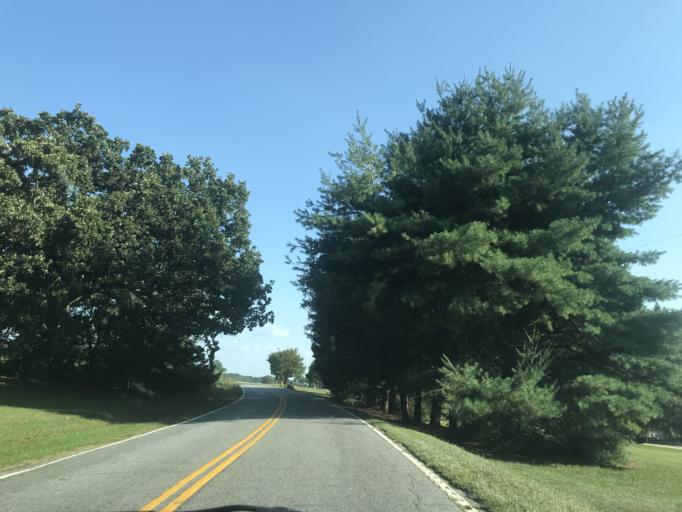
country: US
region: South Carolina
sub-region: Cherokee County
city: Gaffney
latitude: 35.1301
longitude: -81.6903
